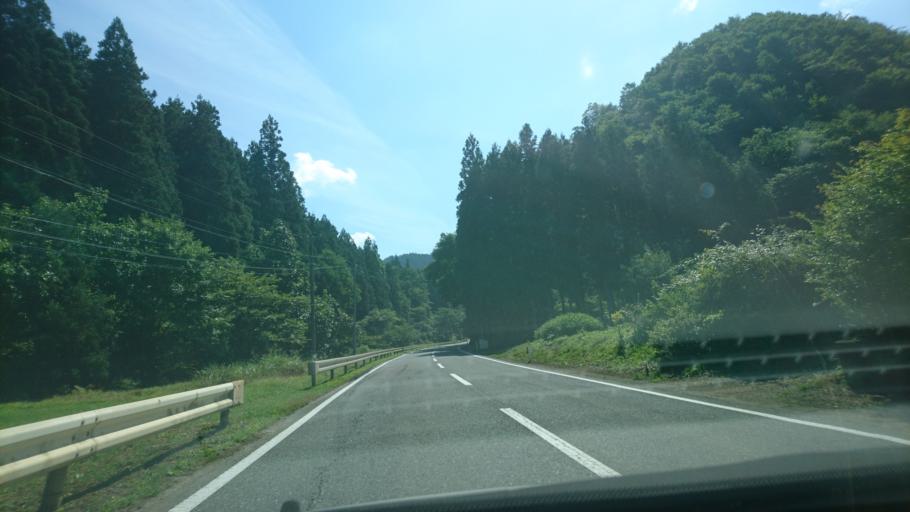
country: JP
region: Iwate
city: Ofunato
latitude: 39.0225
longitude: 141.5000
